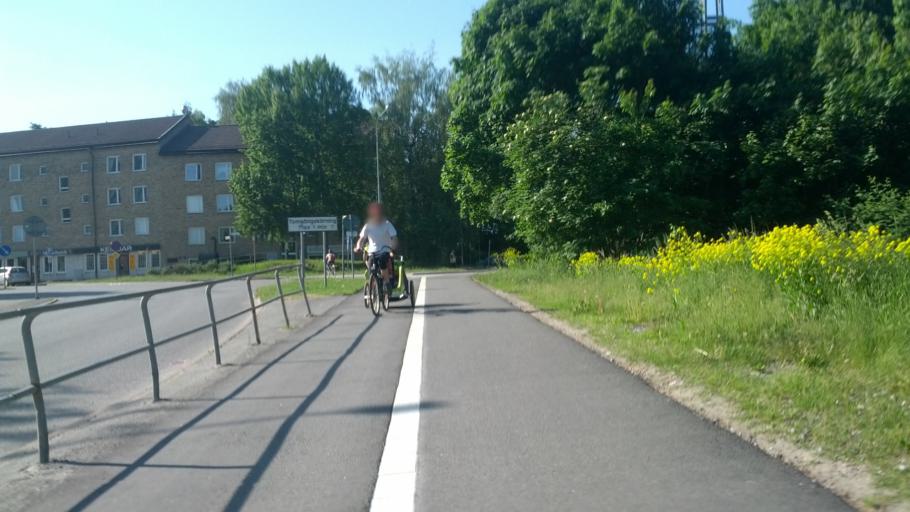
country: SE
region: Stockholm
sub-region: Norrtalje Kommun
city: Bergshamra
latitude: 59.3973
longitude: 18.0339
